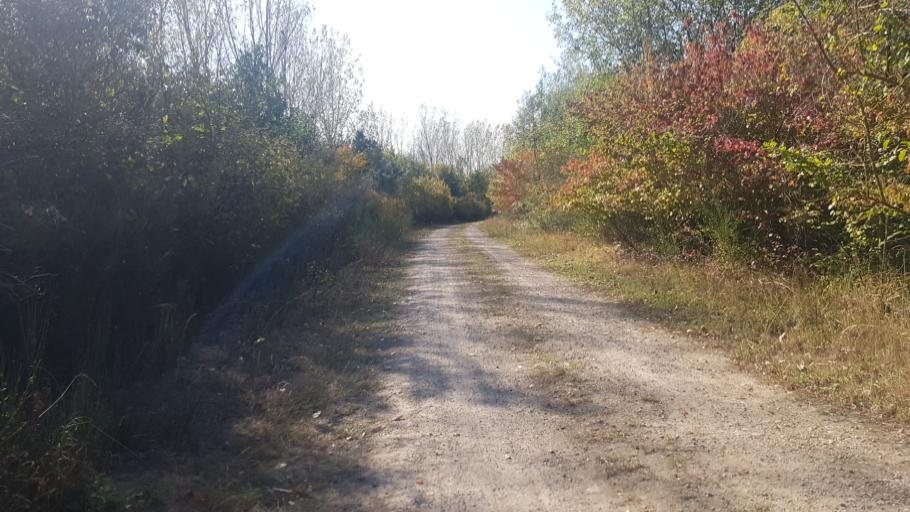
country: DE
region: North Rhine-Westphalia
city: Niedermerz
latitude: 50.8563
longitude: 6.2663
